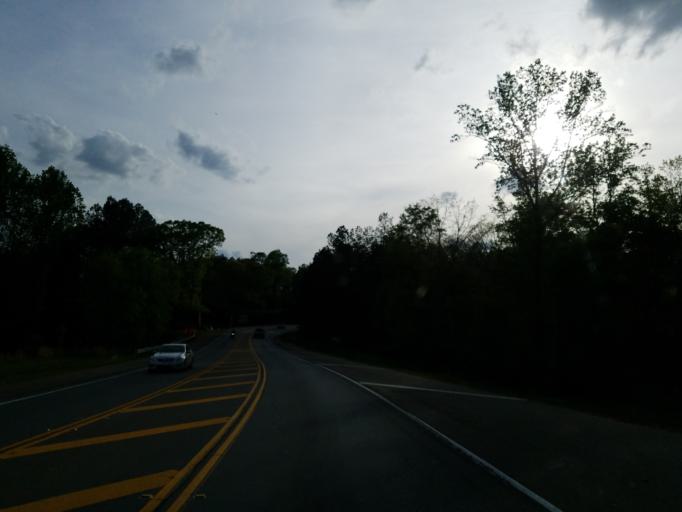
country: US
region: Georgia
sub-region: Cherokee County
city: Ball Ground
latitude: 34.2554
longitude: -84.3432
